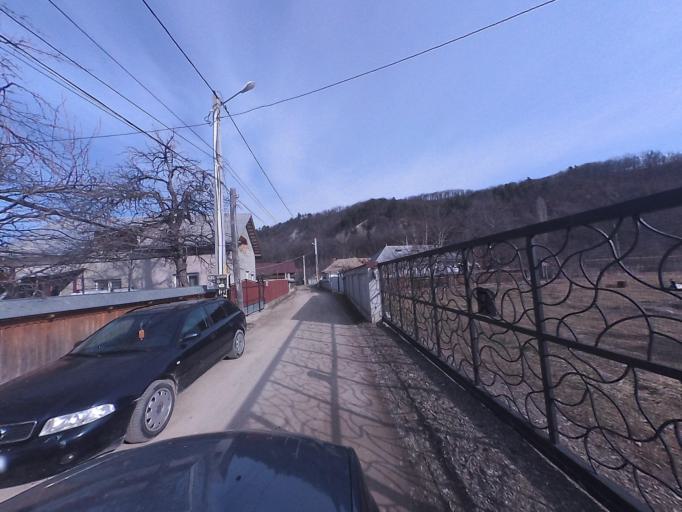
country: RO
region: Neamt
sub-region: Oras Targu Neamt
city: Humulesti
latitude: 47.2142
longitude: 26.3354
